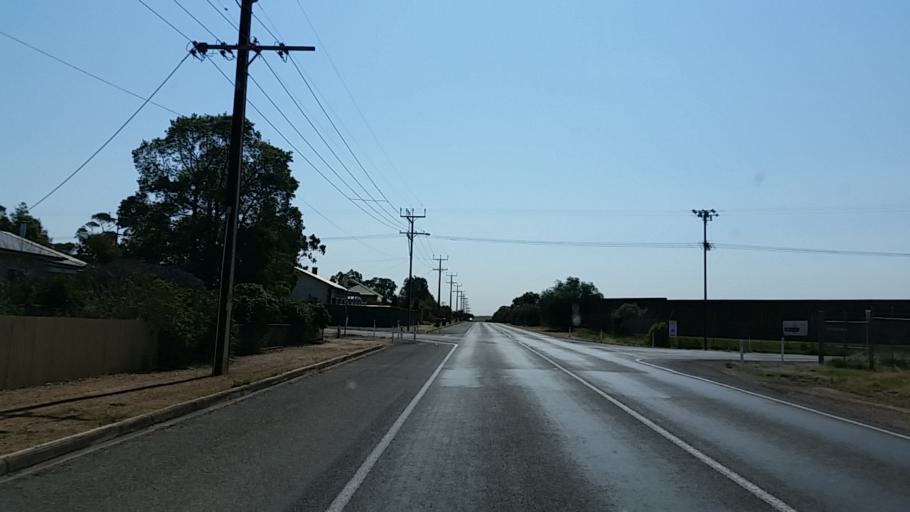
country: AU
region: South Australia
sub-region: Port Pirie City and Dists
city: Crystal Brook
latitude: -33.2619
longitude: 138.3540
